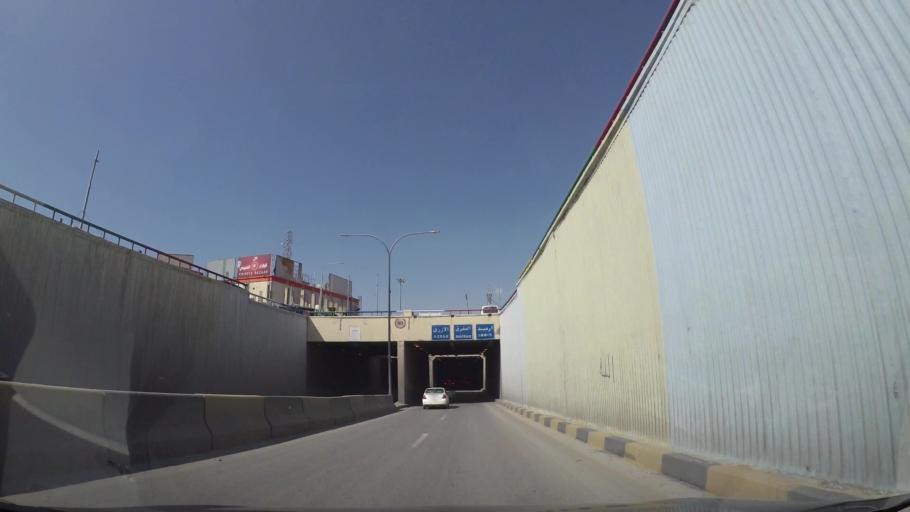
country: JO
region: Zarqa
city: Zarqa
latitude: 32.0598
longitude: 36.0948
